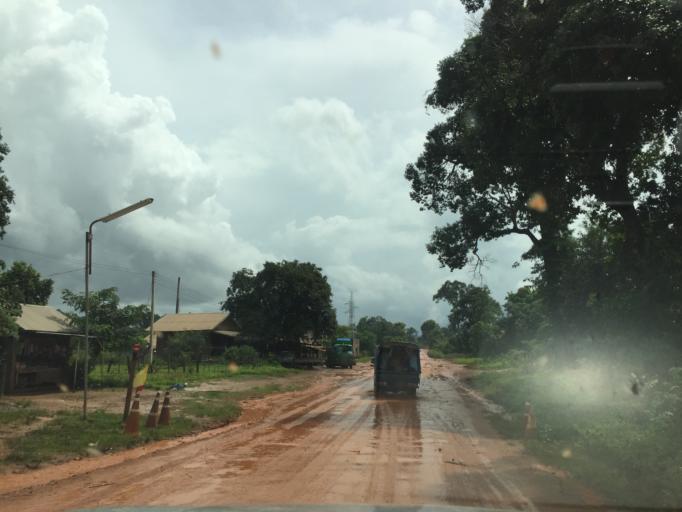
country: LA
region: Attapu
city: Attapu
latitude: 14.8123
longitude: 106.7824
